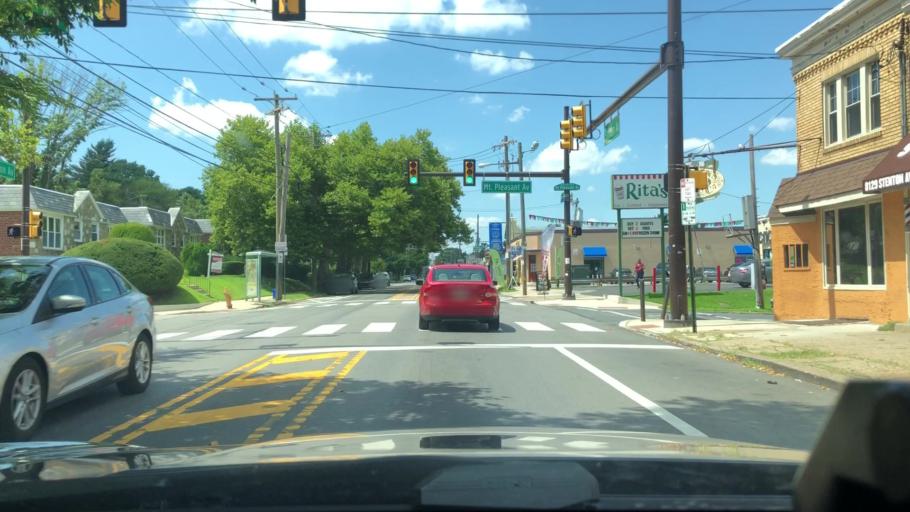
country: US
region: Pennsylvania
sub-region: Montgomery County
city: Wyndmoor
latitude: 40.0671
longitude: -75.1785
